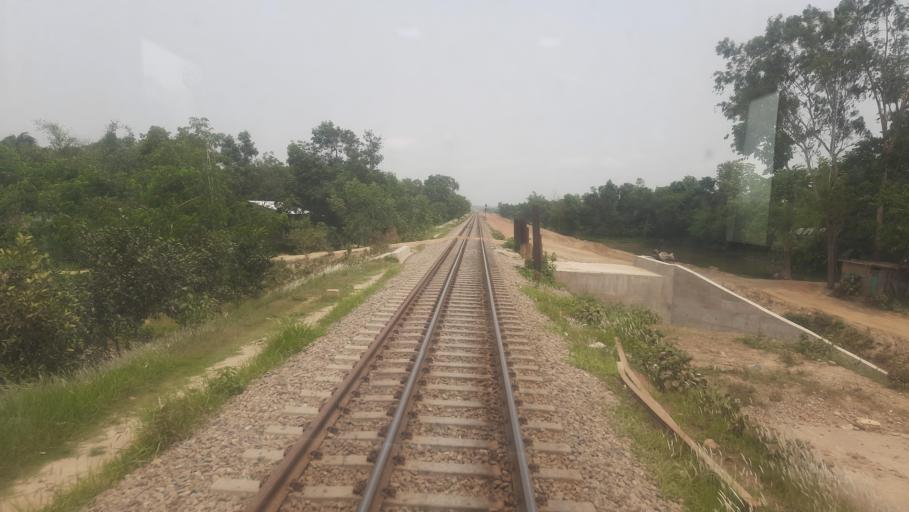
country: BD
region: Chittagong
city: Comilla
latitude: 23.6467
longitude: 91.1474
